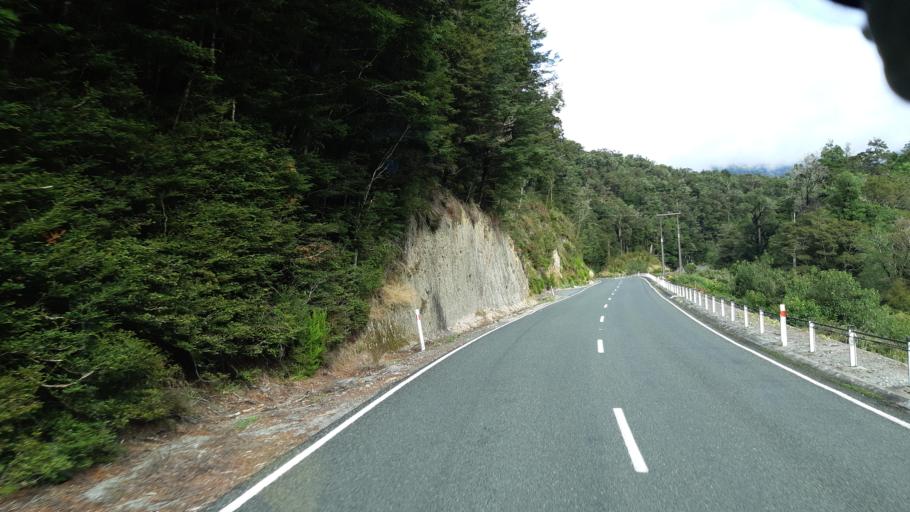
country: NZ
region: West Coast
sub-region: Buller District
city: Westport
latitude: -41.9884
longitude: 172.2161
